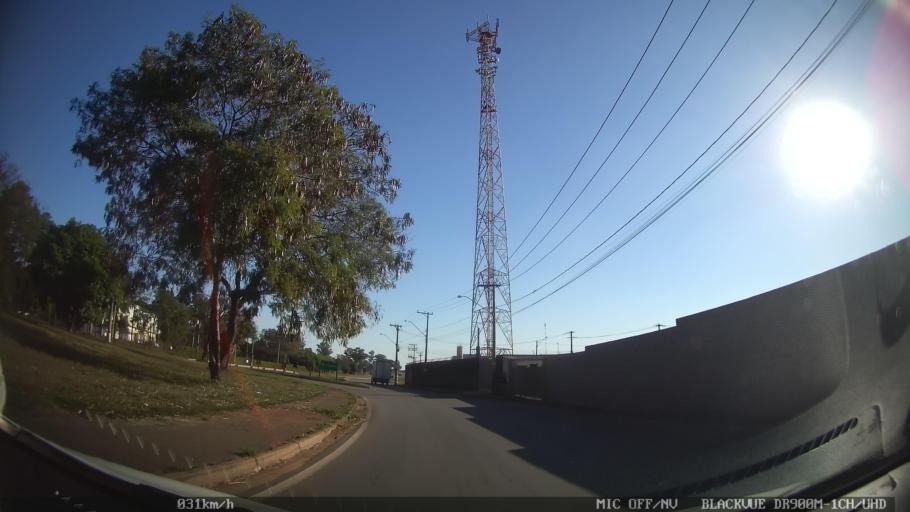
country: BR
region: Sao Paulo
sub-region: Nova Odessa
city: Nova Odessa
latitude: -22.7632
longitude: -47.2555
